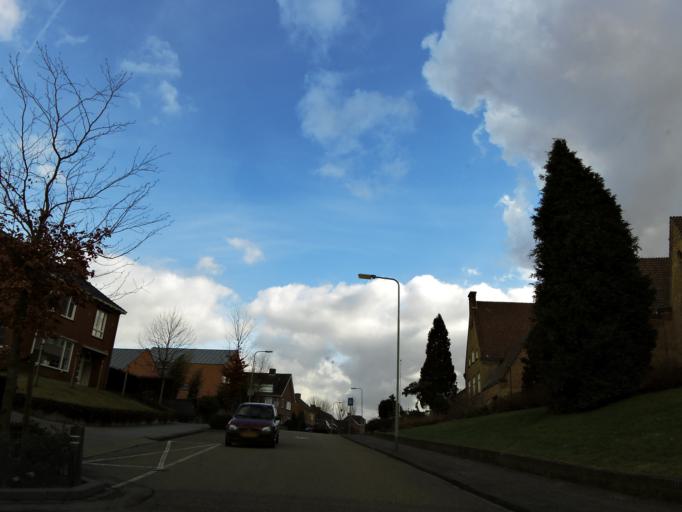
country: NL
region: Limburg
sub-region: Gemeente Onderbanken
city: Merkelbeek
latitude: 50.9703
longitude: 5.9361
